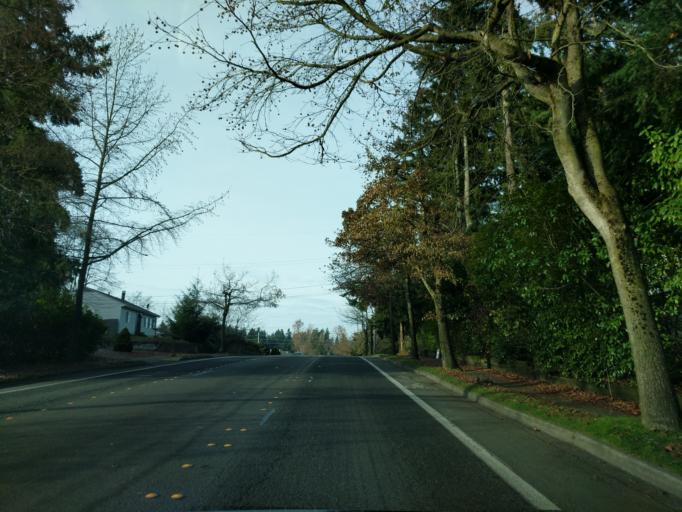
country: US
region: Washington
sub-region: King County
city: Shoreline
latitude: 47.7415
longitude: -122.3413
